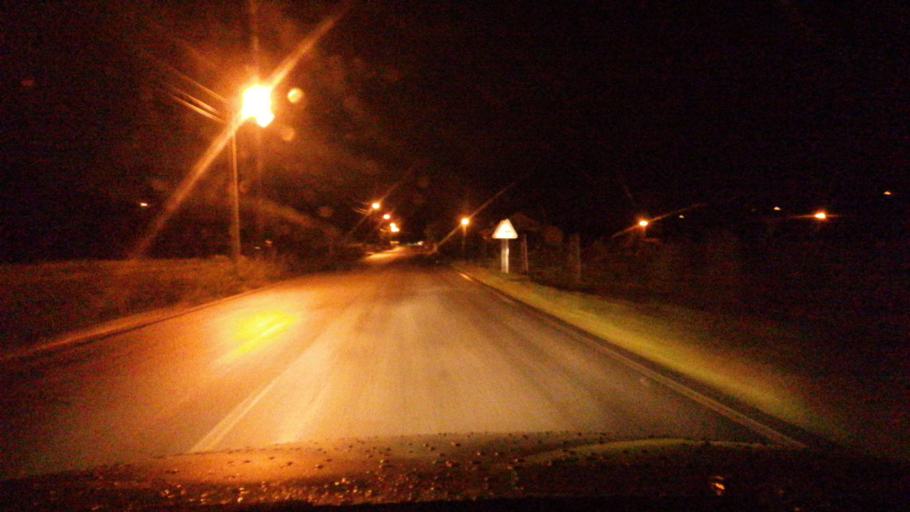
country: PT
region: Viseu
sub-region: Moimenta da Beira
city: Moimenta da Beira
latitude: 40.9481
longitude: -7.5751
